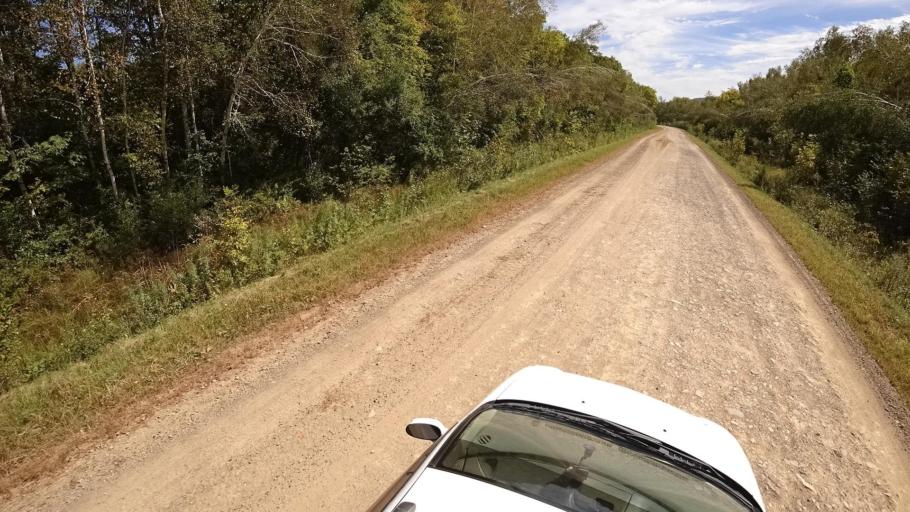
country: RU
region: Primorskiy
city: Yakovlevka
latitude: 44.6618
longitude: 133.7260
